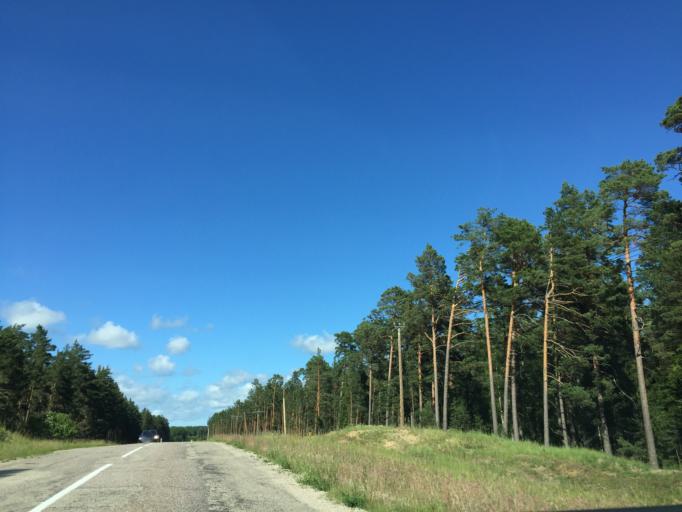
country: LV
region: Ventspils
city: Ventspils
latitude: 57.4792
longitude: 21.6689
